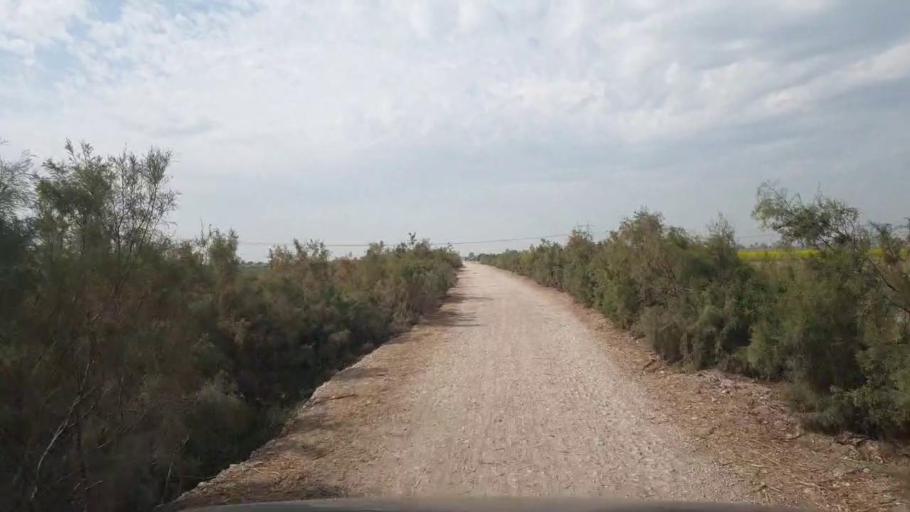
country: PK
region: Sindh
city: Sakrand
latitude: 26.0140
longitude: 68.3896
